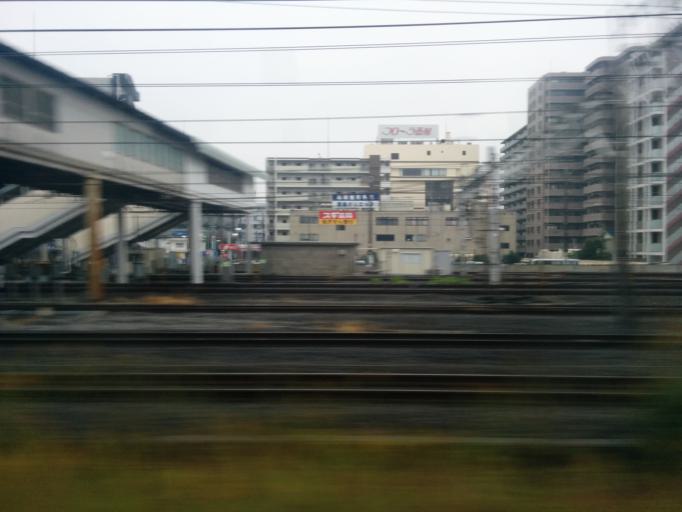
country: JP
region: Chiba
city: Funabashi
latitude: 35.7084
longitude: 139.9576
